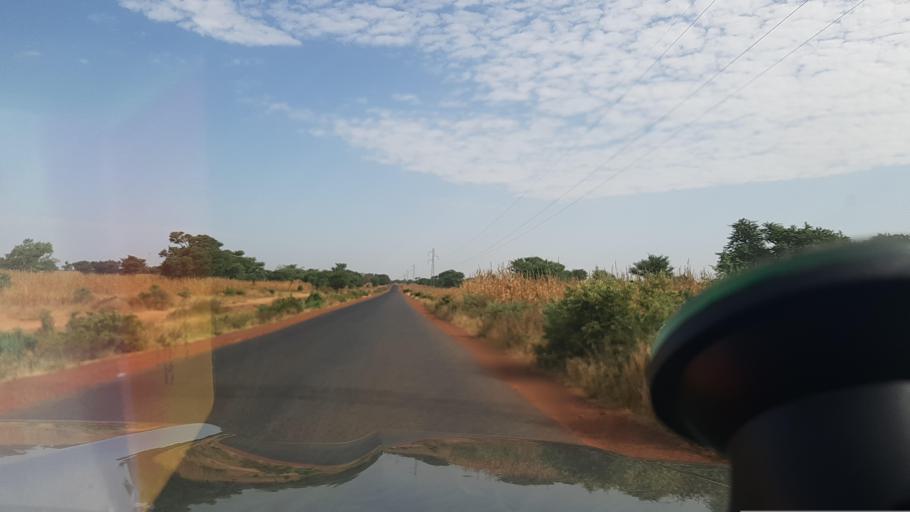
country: ML
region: Segou
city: Markala
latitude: 13.5616
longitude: -6.1114
